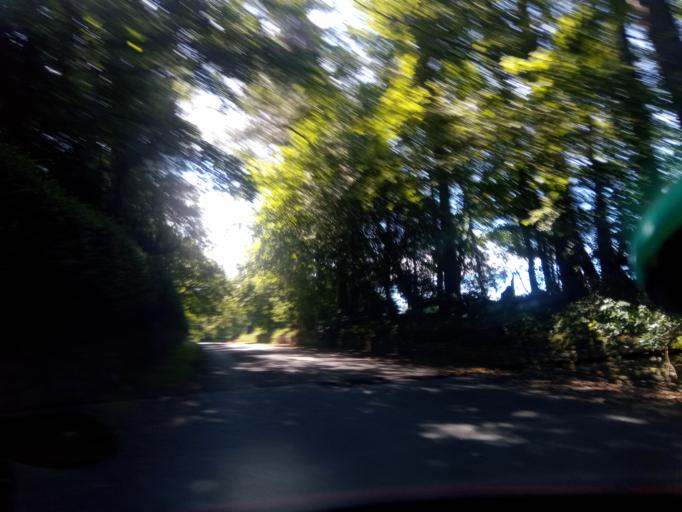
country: GB
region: England
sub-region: Northumberland
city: Bardon Mill
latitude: 54.9038
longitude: -2.3504
